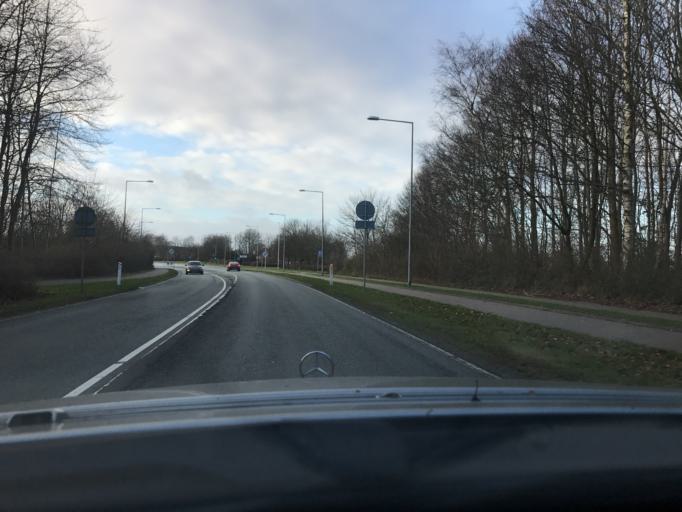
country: DK
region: South Denmark
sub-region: Sonderborg Kommune
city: Nordborg
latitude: 55.0546
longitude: 9.7616
